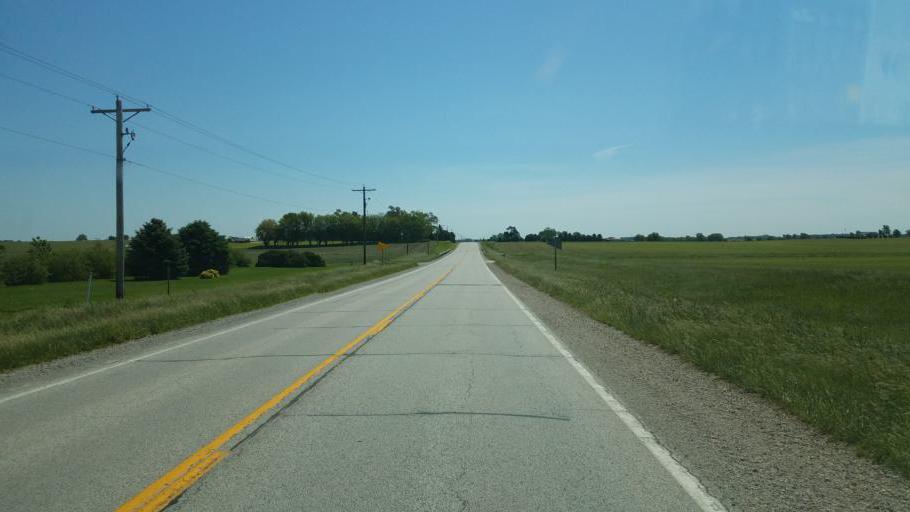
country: US
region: Illinois
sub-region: McLean County
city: Heyworth
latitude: 40.3120
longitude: -89.0688
